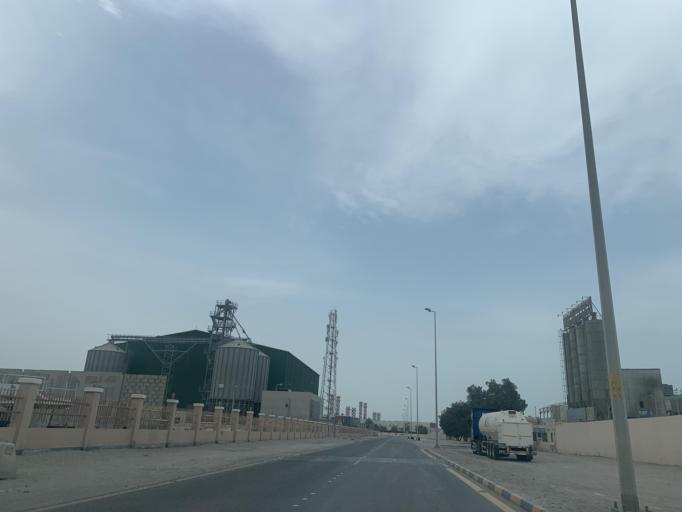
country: BH
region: Muharraq
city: Al Hadd
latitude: 26.2079
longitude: 50.6623
